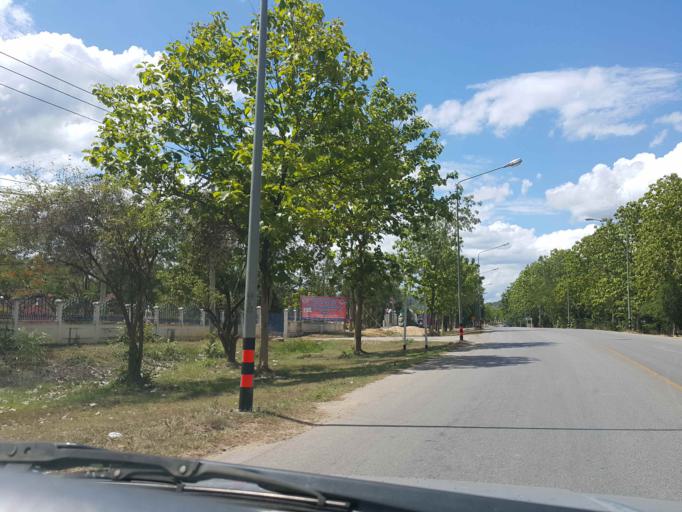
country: TH
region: Chiang Mai
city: Chom Thong
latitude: 18.4577
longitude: 98.6753
